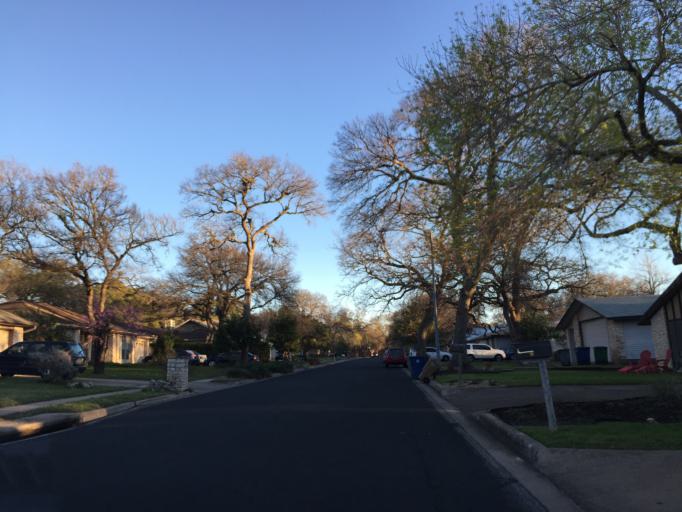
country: US
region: Texas
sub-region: Williamson County
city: Jollyville
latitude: 30.4307
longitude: -97.7779
